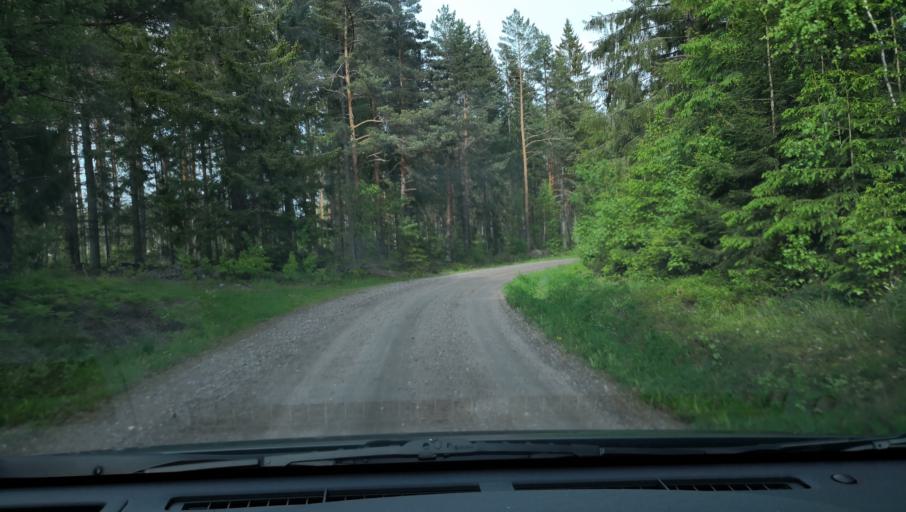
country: SE
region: Vaestmanland
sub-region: Arboga Kommun
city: Tyringe
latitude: 59.3632
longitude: 15.9728
